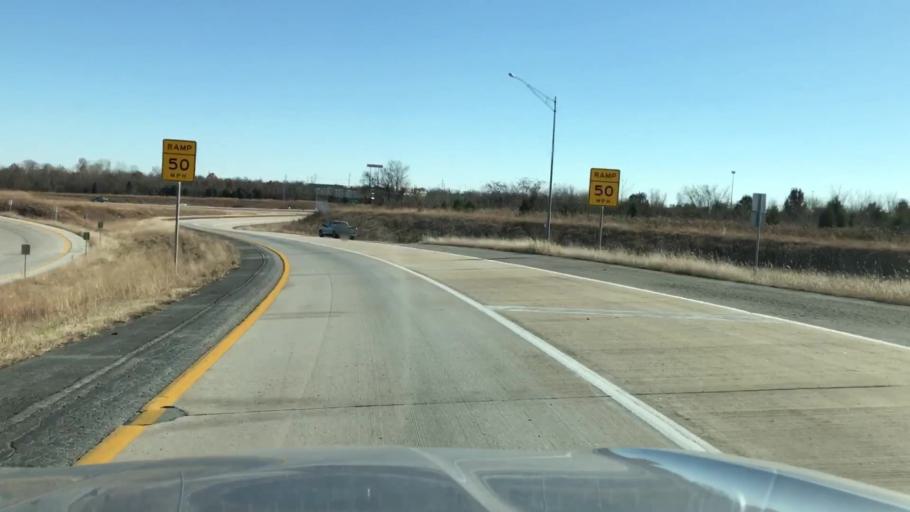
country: US
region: Missouri
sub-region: Jasper County
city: Duenweg
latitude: 37.0595
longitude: -94.4295
